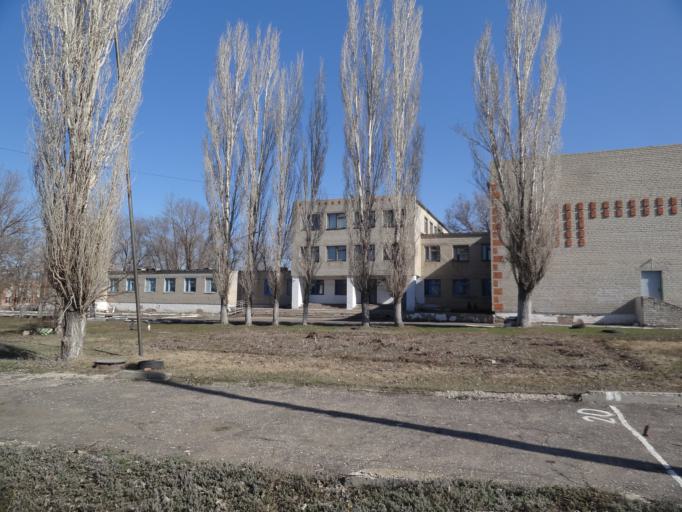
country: RU
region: Saratov
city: Shumeyka
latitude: 51.3892
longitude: 46.3040
